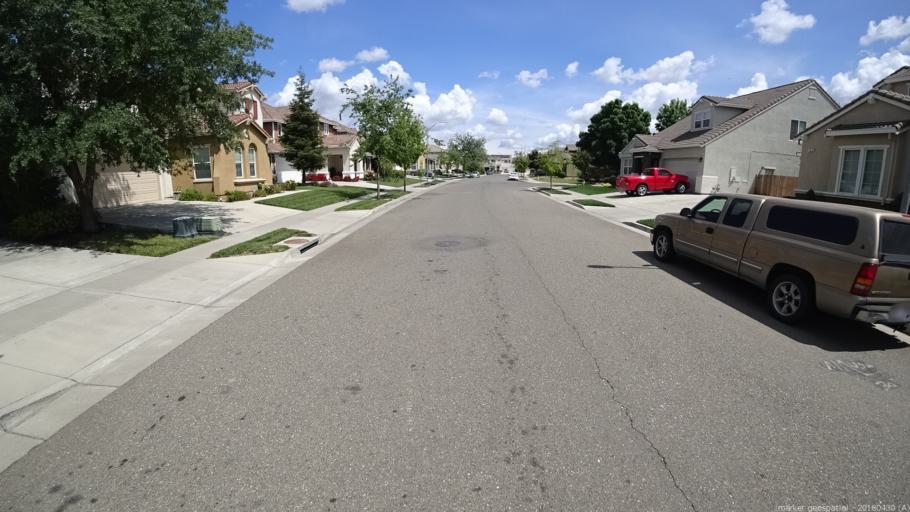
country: US
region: California
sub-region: Yolo County
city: West Sacramento
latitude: 38.5509
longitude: -121.5236
